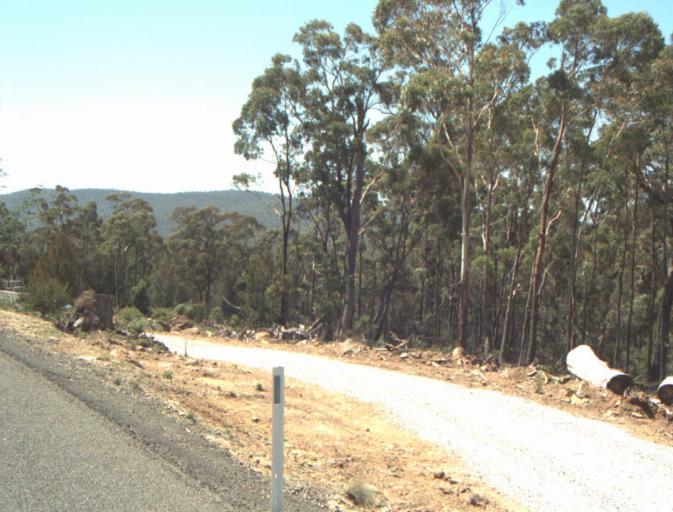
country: AU
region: Tasmania
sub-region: Launceston
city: Mayfield
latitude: -41.3201
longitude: 147.1227
